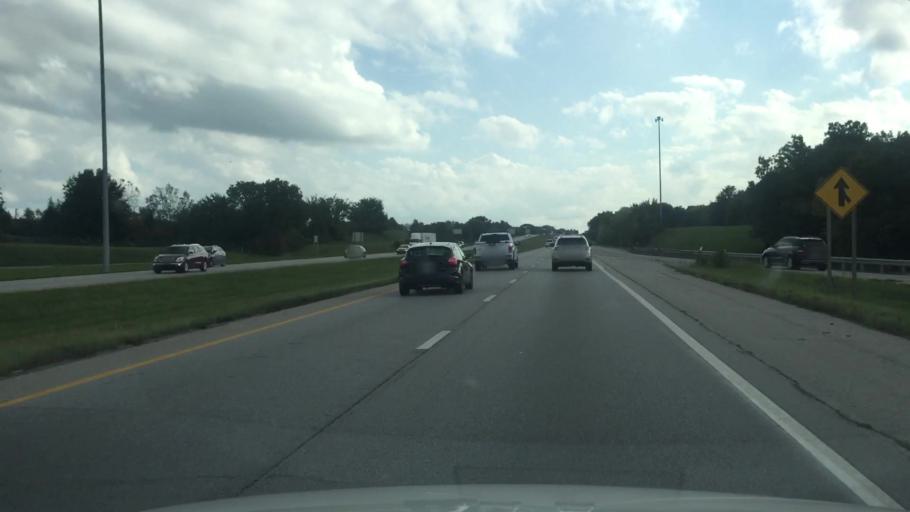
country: US
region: Kansas
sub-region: Johnson County
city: Lenexa
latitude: 38.8815
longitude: -94.6766
